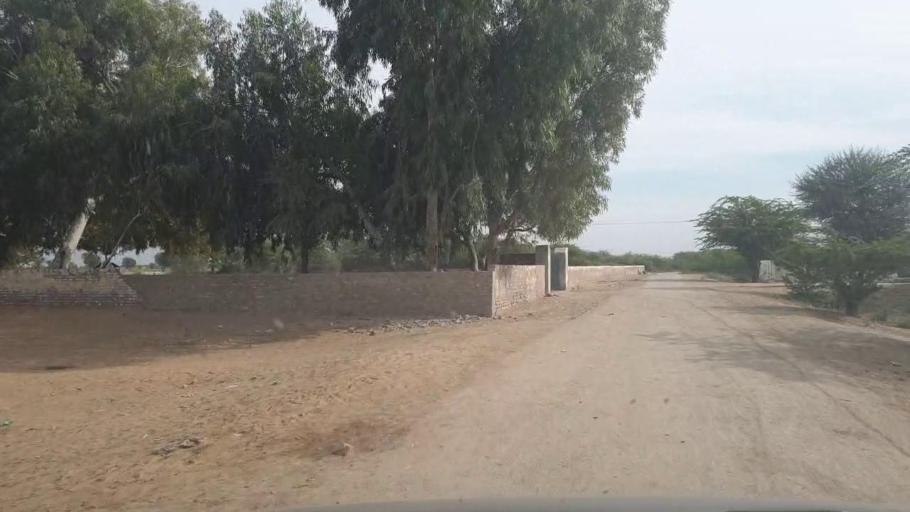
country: PK
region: Sindh
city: Kunri
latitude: 25.2873
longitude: 69.5987
